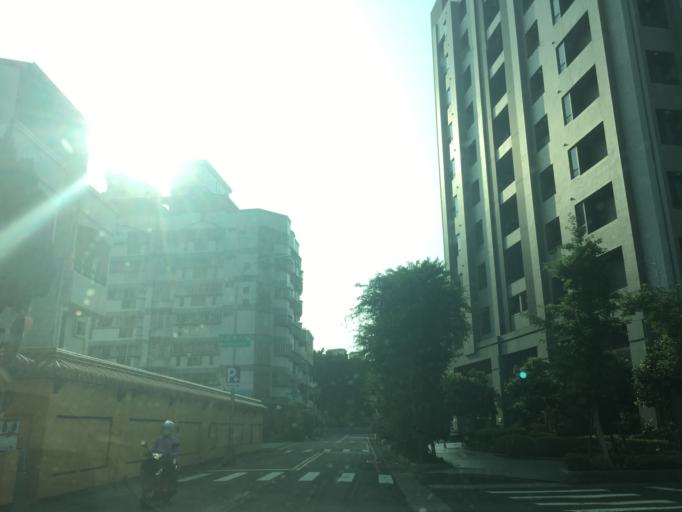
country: TW
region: Taiwan
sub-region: Taichung City
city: Taichung
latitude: 24.1677
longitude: 120.6897
